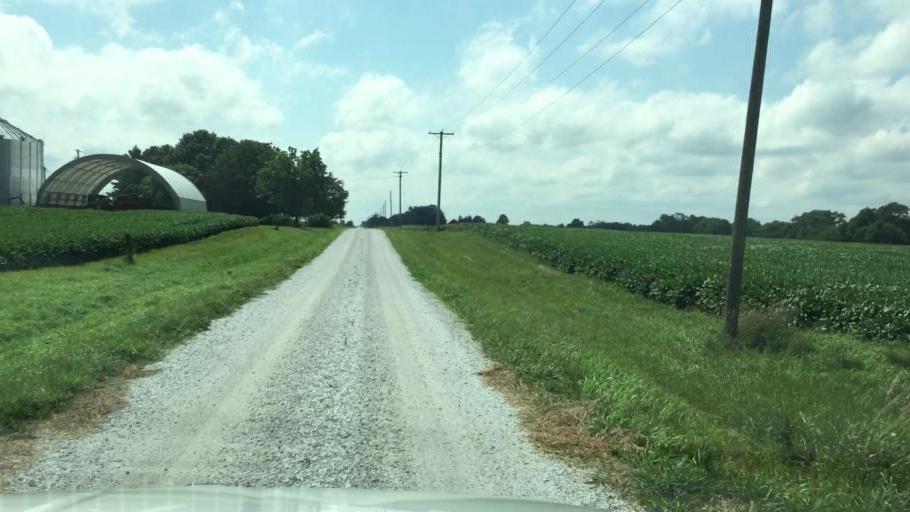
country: US
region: Illinois
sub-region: Hancock County
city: Carthage
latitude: 40.5356
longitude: -91.1637
